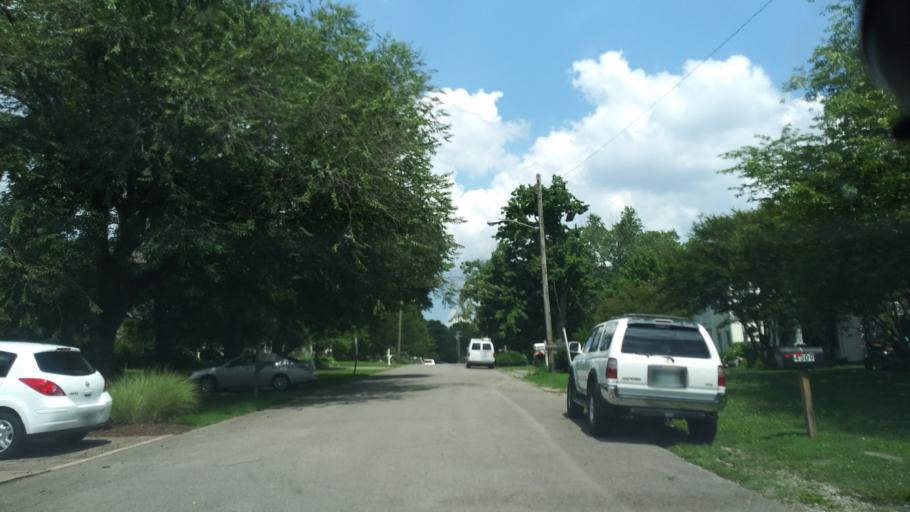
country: US
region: Tennessee
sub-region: Davidson County
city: Belle Meade
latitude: 36.1488
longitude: -86.8391
